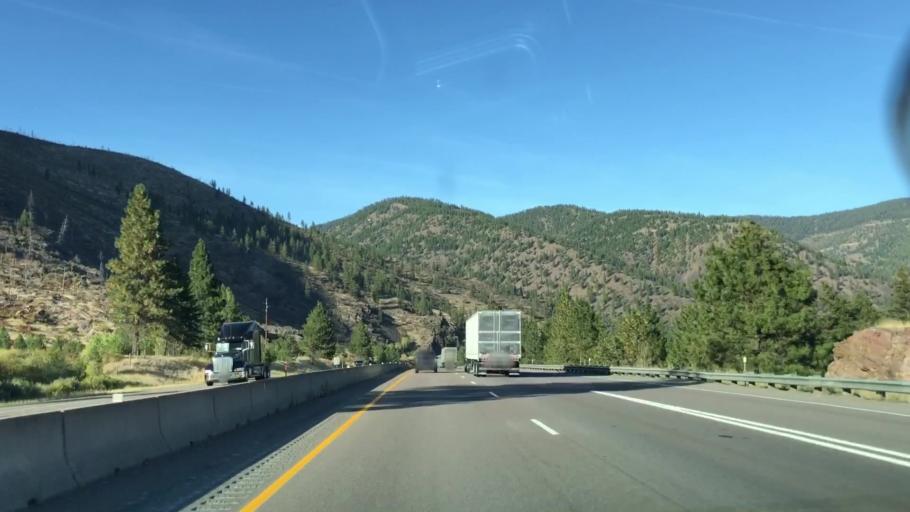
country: US
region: Montana
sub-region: Missoula County
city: Frenchtown
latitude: 47.0140
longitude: -114.5426
